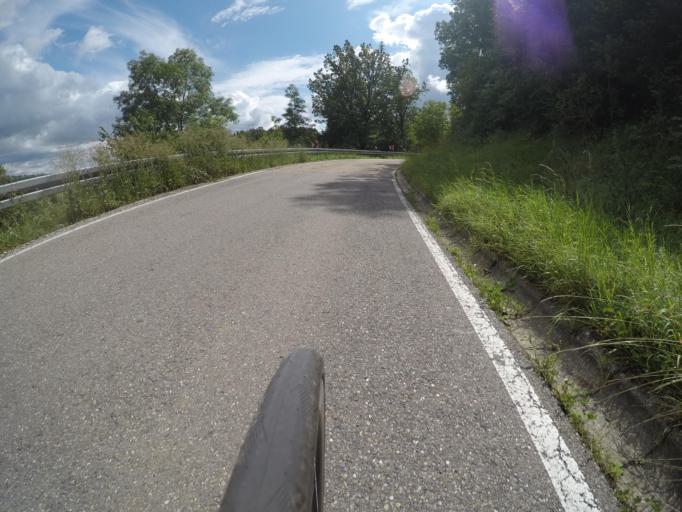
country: DE
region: Baden-Wuerttemberg
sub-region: Karlsruhe Region
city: Gechingen
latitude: 48.6755
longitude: 8.8530
